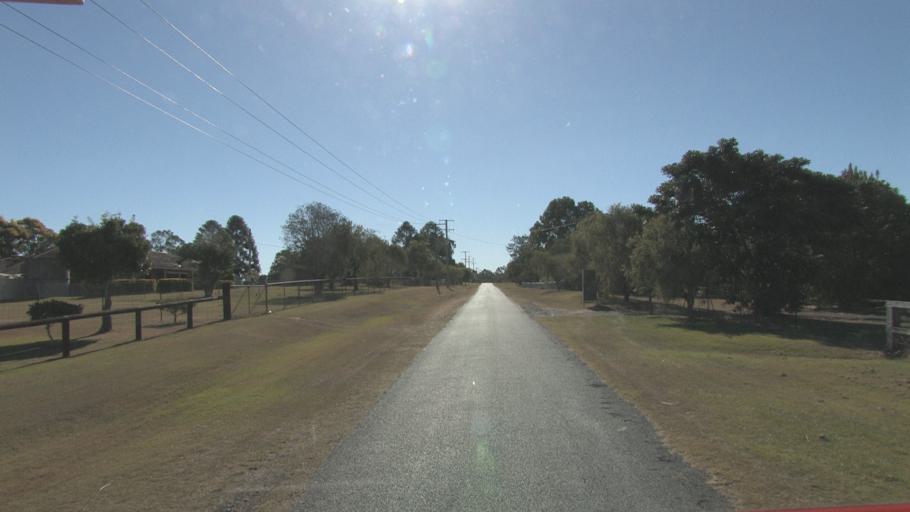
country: AU
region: Queensland
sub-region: Logan
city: North Maclean
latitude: -27.7853
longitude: 153.0201
